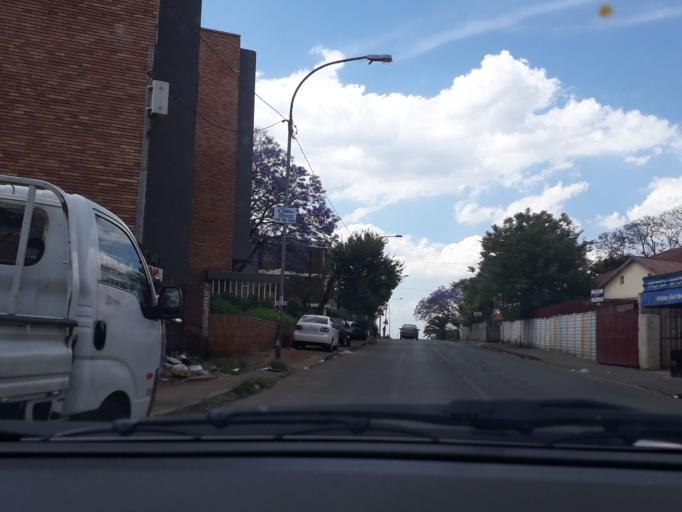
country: ZA
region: Gauteng
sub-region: City of Johannesburg Metropolitan Municipality
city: Johannesburg
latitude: -26.1768
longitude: 28.0709
